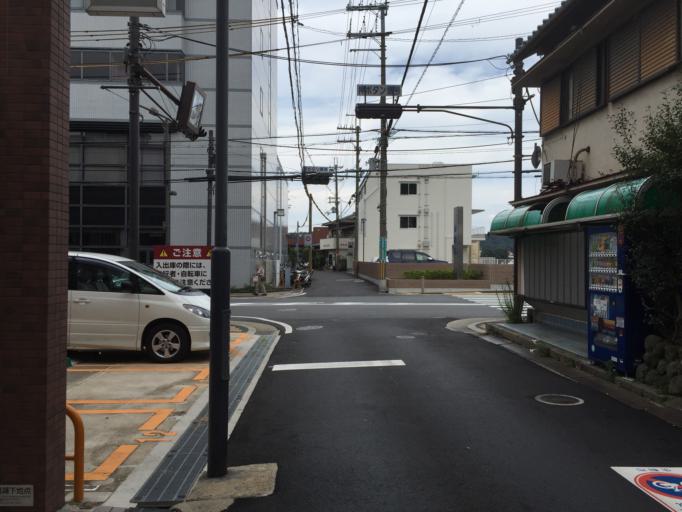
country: JP
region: Nara
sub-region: Ikoma-shi
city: Ikoma
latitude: 34.6916
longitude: 135.6982
